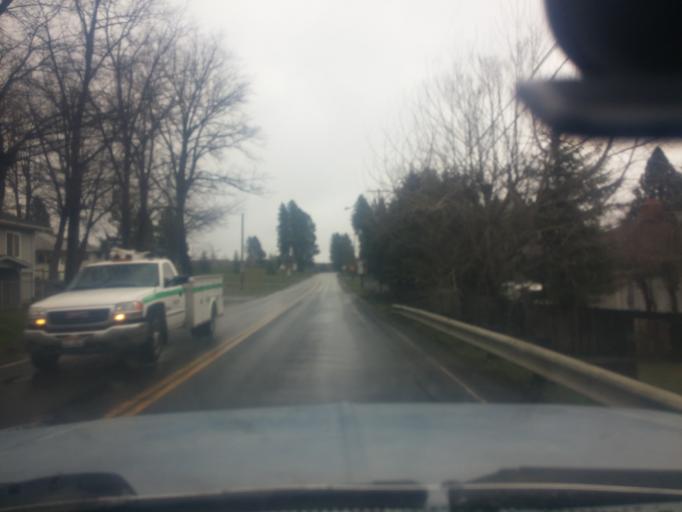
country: US
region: Idaho
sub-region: Latah County
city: Moscow
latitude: 46.9215
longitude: -116.8938
